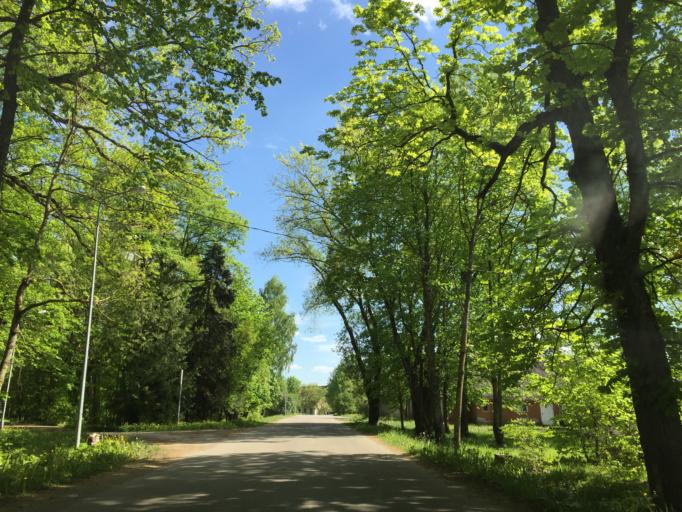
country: LV
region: Bauskas Rajons
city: Bauska
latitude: 56.3934
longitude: 24.1265
